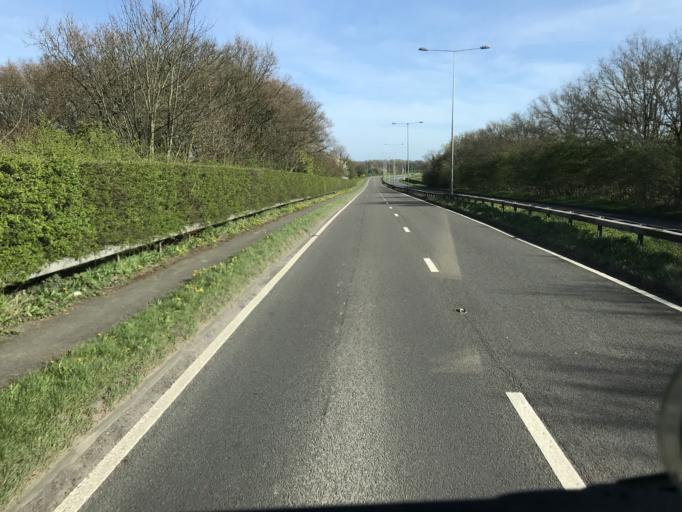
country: GB
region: England
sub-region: Cheshire West and Chester
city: Marston
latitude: 53.2685
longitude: -2.4556
